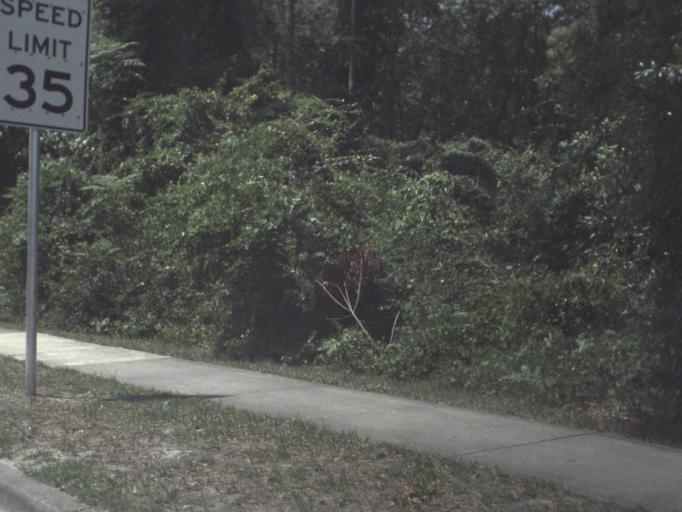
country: US
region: Florida
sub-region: Duval County
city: Jacksonville
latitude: 30.4316
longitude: -81.6741
